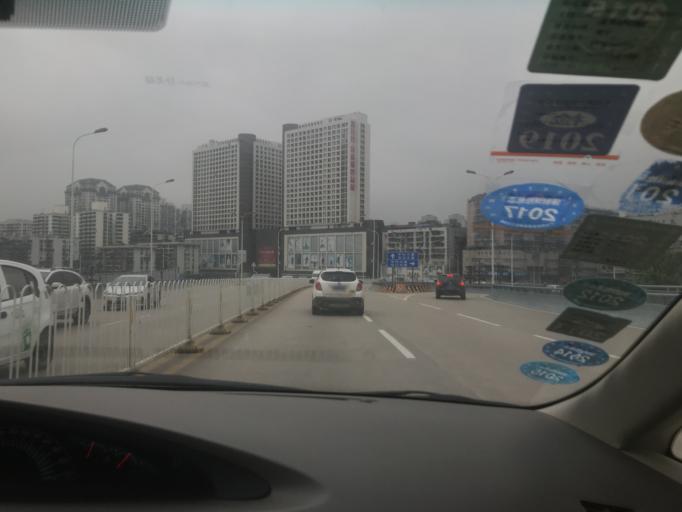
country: CN
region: Hubei
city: Wuhan
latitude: 30.5672
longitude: 114.2776
